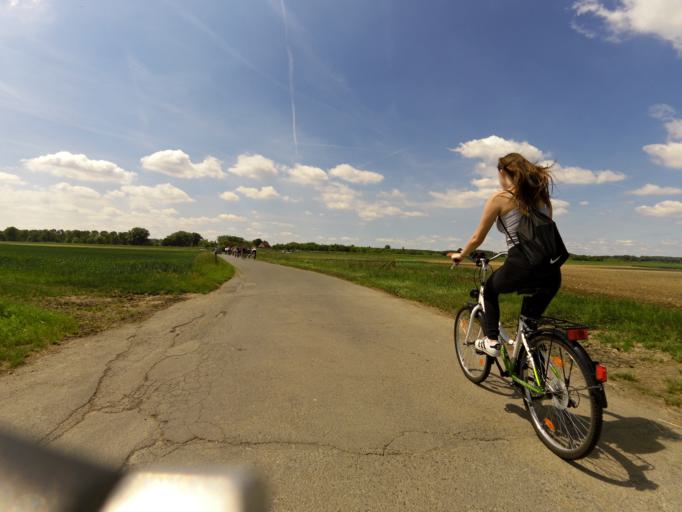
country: DE
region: Rheinland-Pfalz
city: Nackenheim
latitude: 49.9181
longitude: 8.3726
